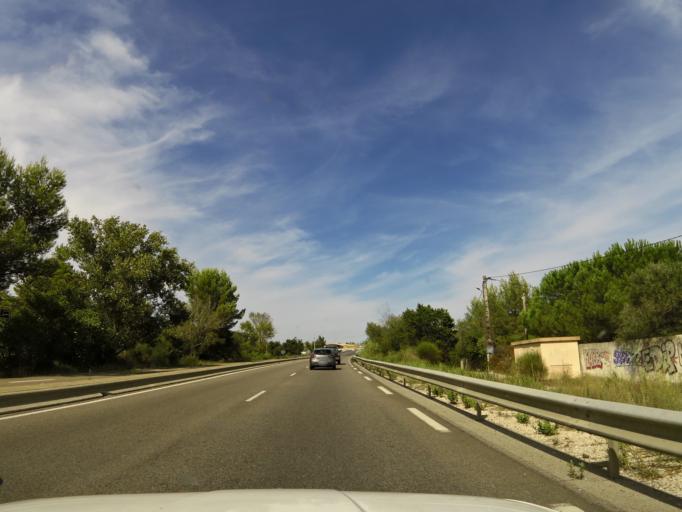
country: FR
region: Languedoc-Roussillon
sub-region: Departement du Gard
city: Nimes
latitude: 43.8524
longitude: 4.3202
